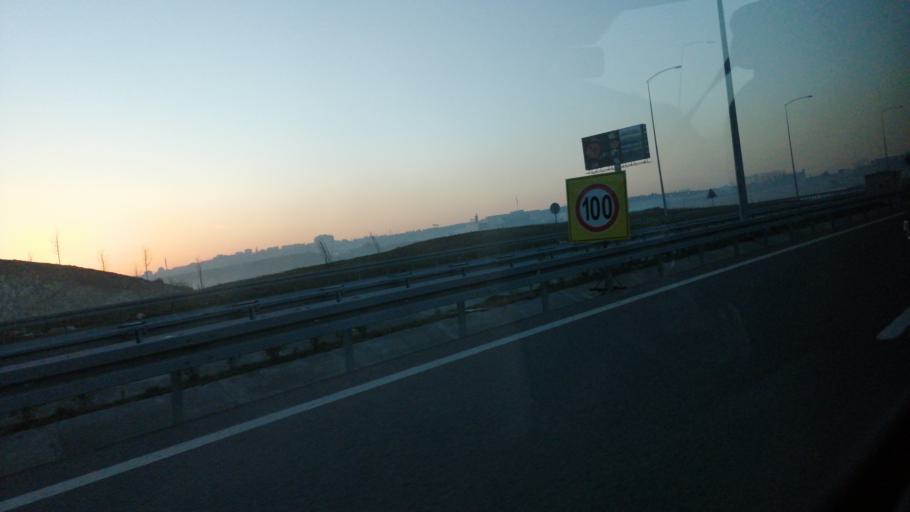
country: TR
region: Kocaeli
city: Tavsanli
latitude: 40.7936
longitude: 29.5117
